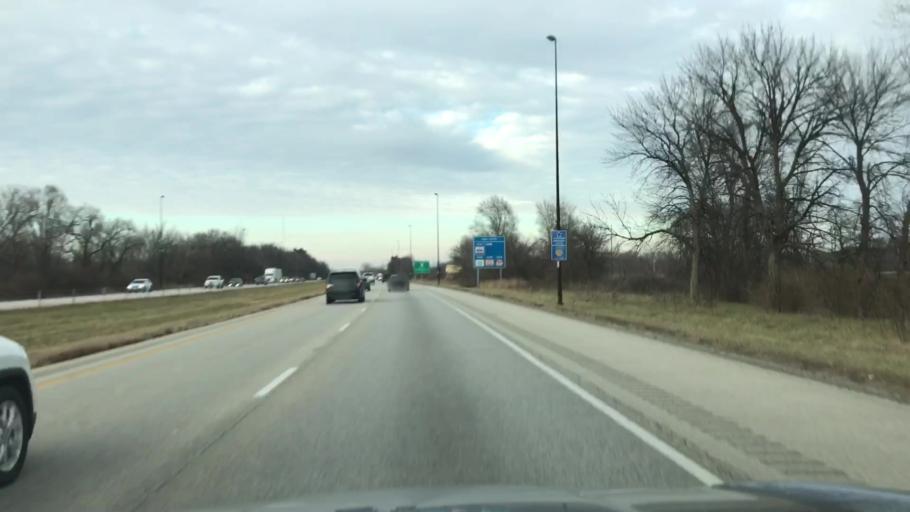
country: US
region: Illinois
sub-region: Sangamon County
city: Grandview
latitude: 39.8106
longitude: -89.5929
